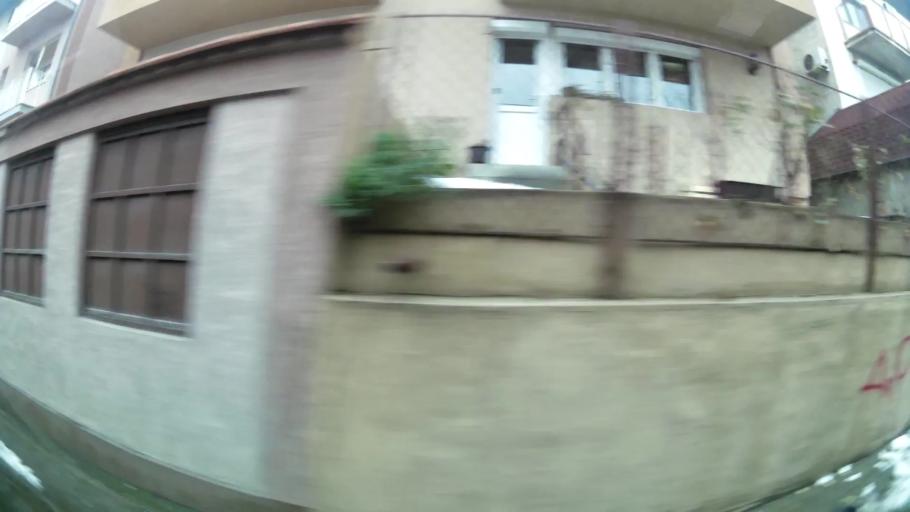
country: RS
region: Central Serbia
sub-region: Belgrade
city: Vozdovac
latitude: 44.7807
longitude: 20.4793
